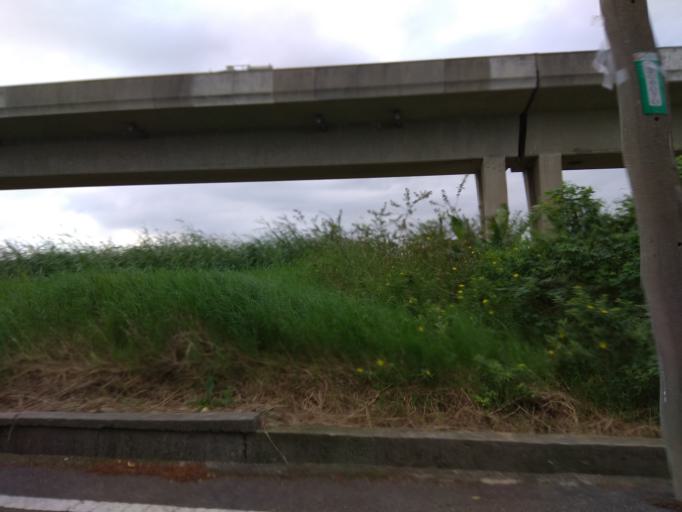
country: TW
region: Taiwan
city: Taoyuan City
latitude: 25.0448
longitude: 121.2151
